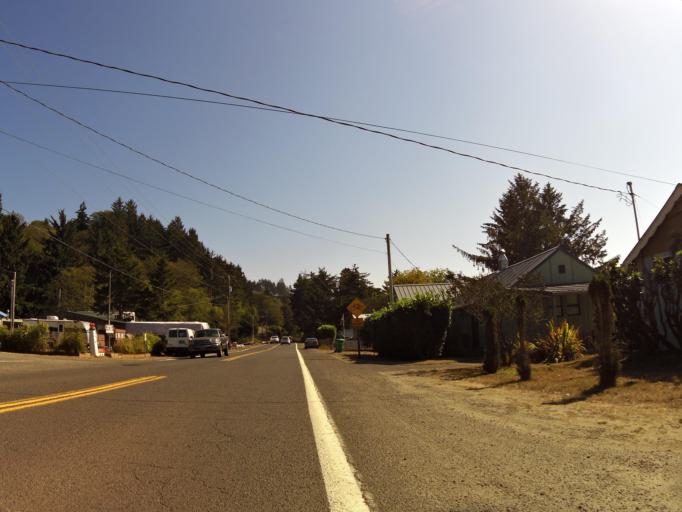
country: US
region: Oregon
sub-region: Tillamook County
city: Pacific City
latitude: 45.1969
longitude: -123.9582
